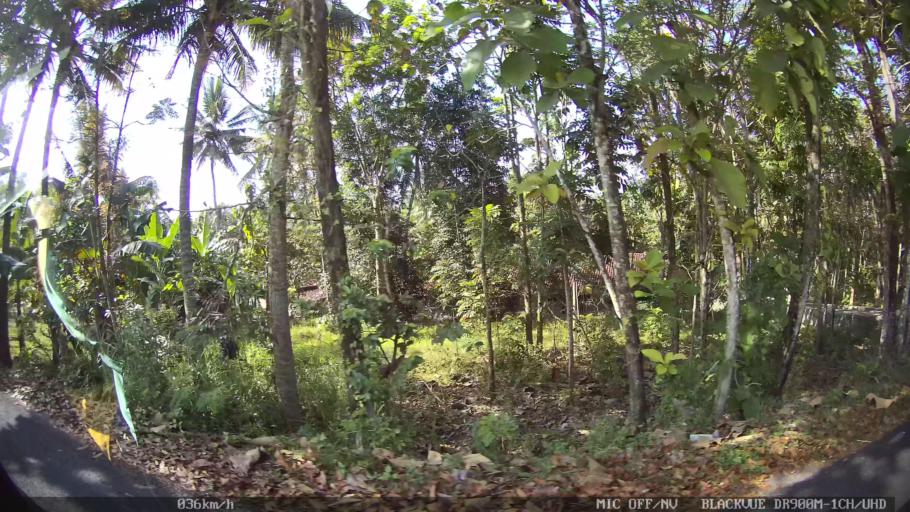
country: ID
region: Daerah Istimewa Yogyakarta
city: Kasihan
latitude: -7.8177
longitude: 110.2958
